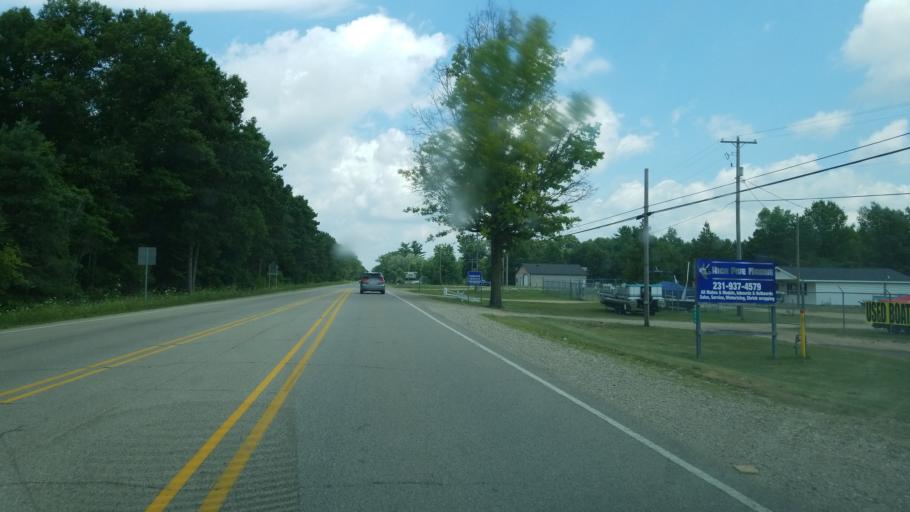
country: US
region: Michigan
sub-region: Montcalm County
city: Howard City
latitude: 43.4111
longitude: -85.4659
